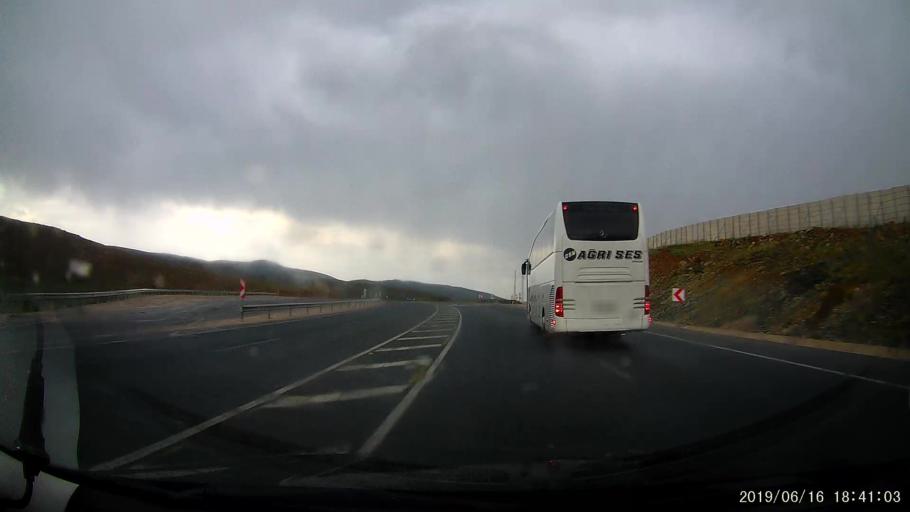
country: TR
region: Erzincan
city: Catalarmut
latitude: 39.8780
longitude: 39.1336
